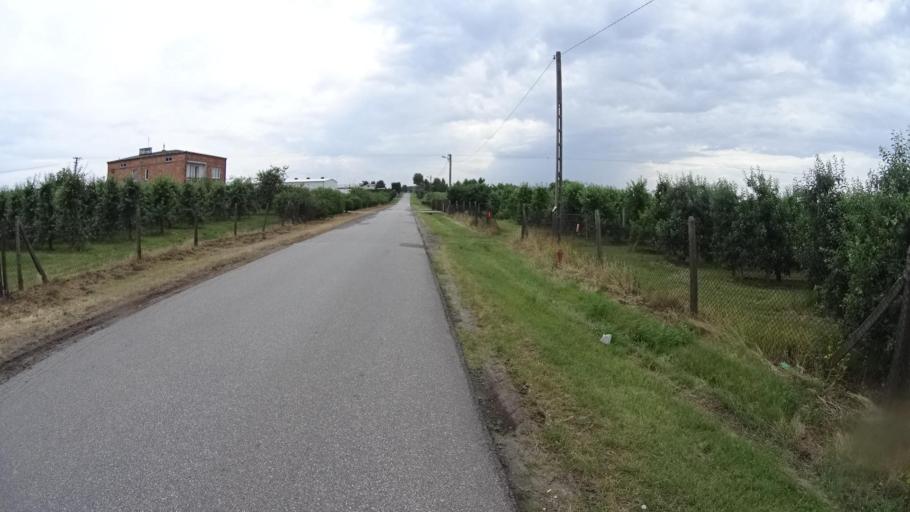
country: PL
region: Masovian Voivodeship
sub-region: Powiat grojecki
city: Belsk Duzy
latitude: 51.7967
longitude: 20.8585
